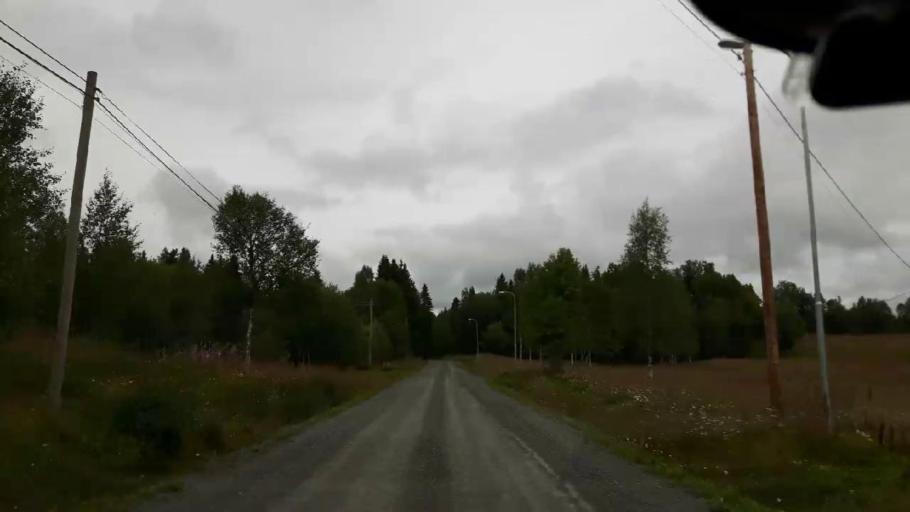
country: SE
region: Jaemtland
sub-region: Krokoms Kommun
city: Valla
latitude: 63.6999
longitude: 13.8727
